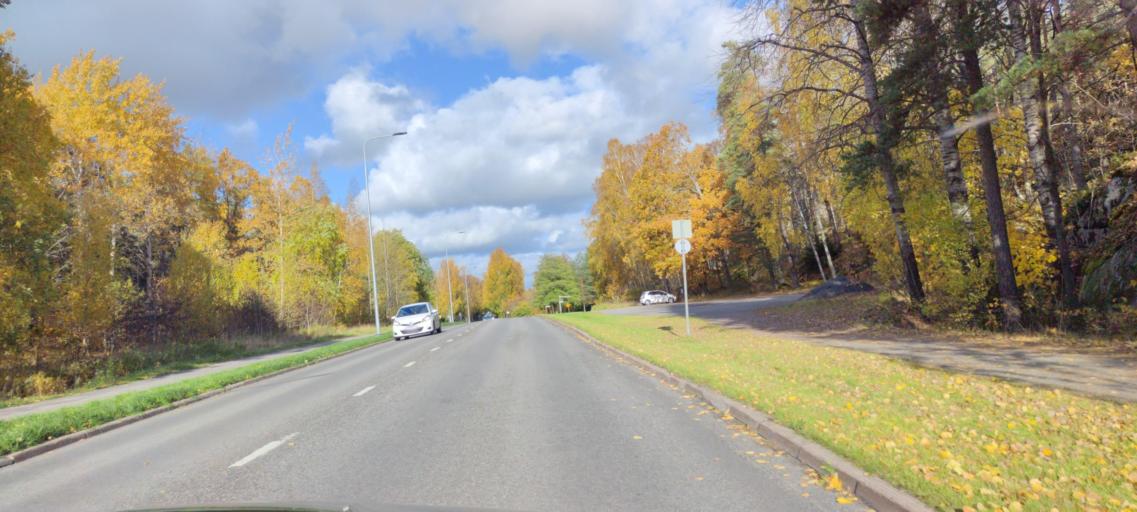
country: FI
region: Varsinais-Suomi
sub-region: Turku
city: Turku
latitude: 60.4168
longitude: 22.2693
